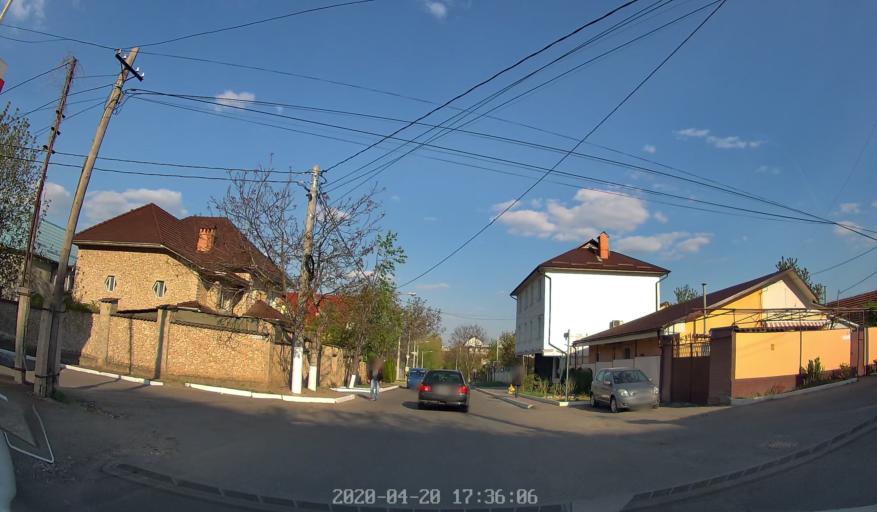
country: MD
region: Chisinau
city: Chisinau
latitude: 46.9891
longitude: 28.8613
